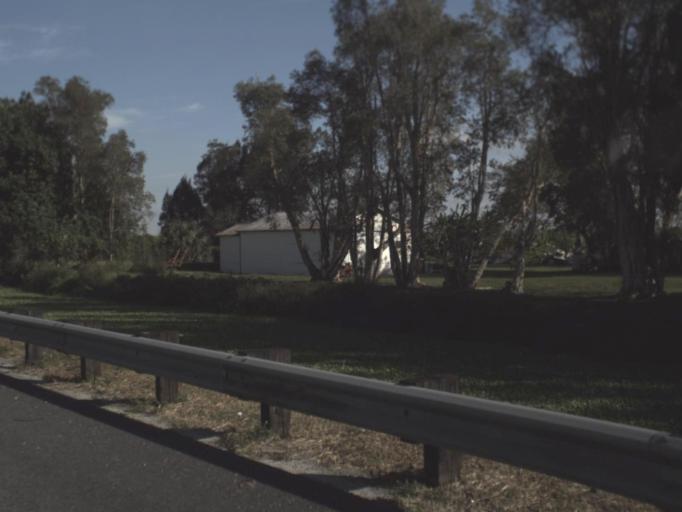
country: US
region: Florida
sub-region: Hendry County
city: Harlem
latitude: 26.7541
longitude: -80.9947
